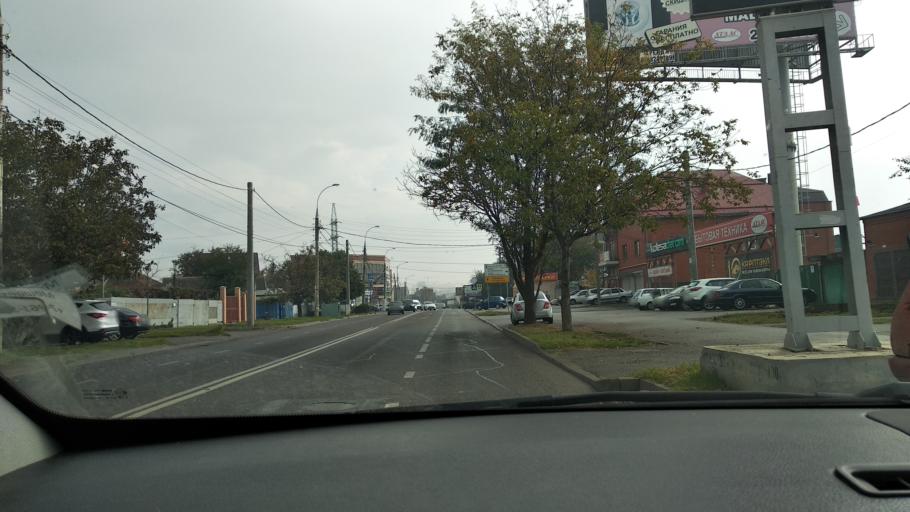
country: RU
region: Krasnodarskiy
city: Krasnodar
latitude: 45.0275
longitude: 39.0246
